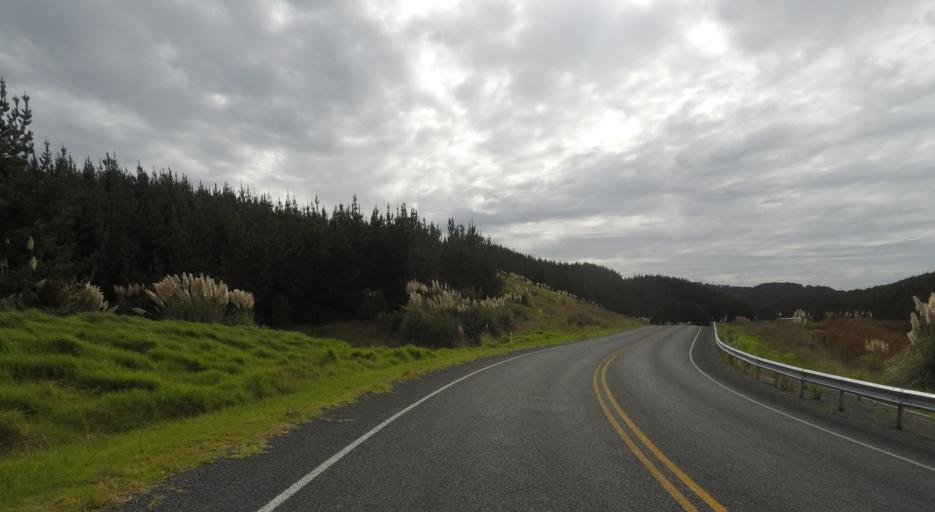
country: NZ
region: Auckland
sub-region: Auckland
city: Rothesay Bay
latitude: -36.6551
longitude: 174.6998
